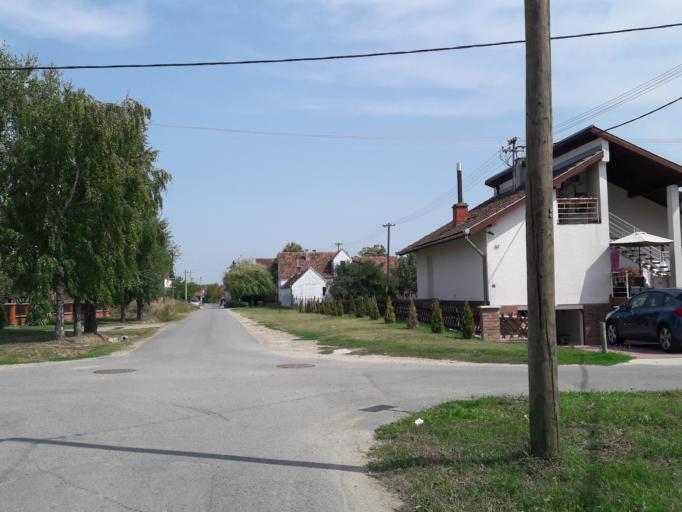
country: HR
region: Osjecko-Baranjska
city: Visnjevac
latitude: 45.5252
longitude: 18.6239
